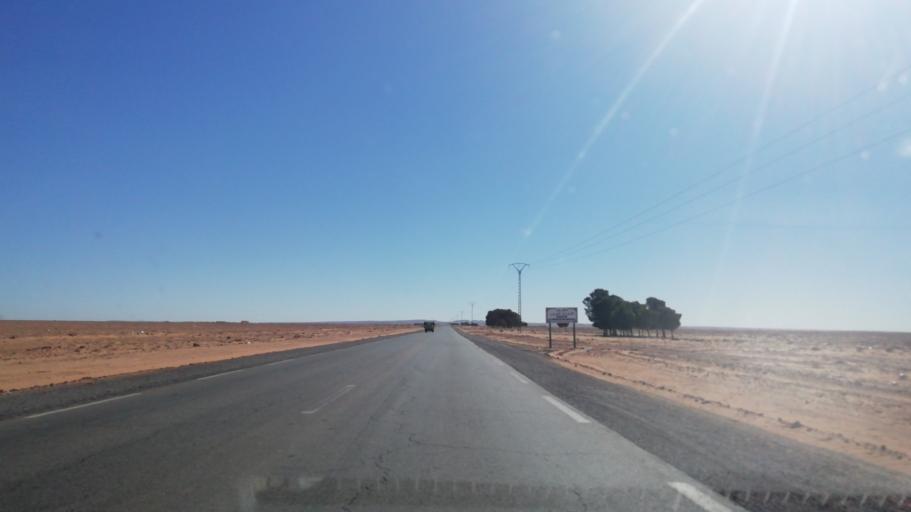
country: DZ
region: Saida
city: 'Ain el Hadjar
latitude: 34.0093
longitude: 0.1195
